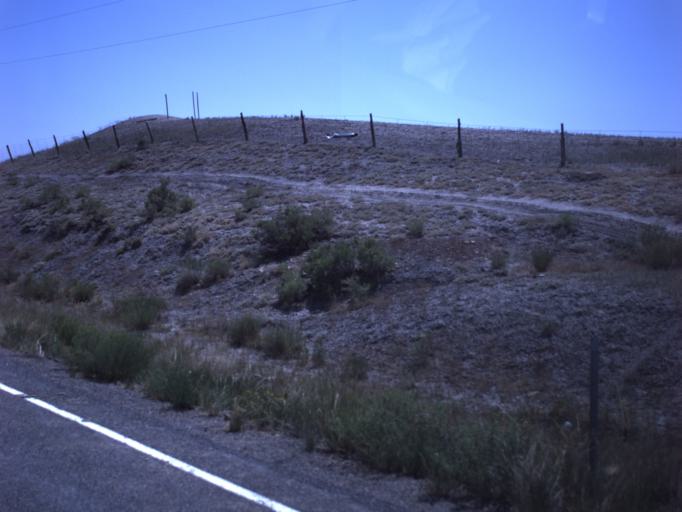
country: US
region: Utah
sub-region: Emery County
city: Orangeville
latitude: 39.2127
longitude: -111.0545
